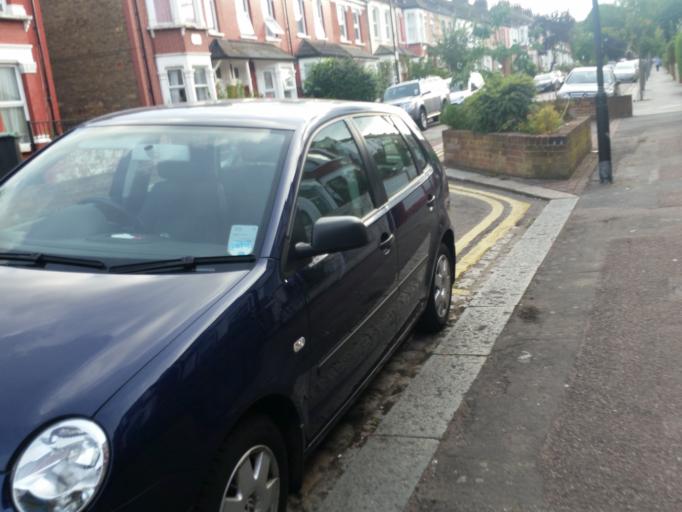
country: GB
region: England
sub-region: Greater London
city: Harringay
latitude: 51.5853
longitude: -0.1036
